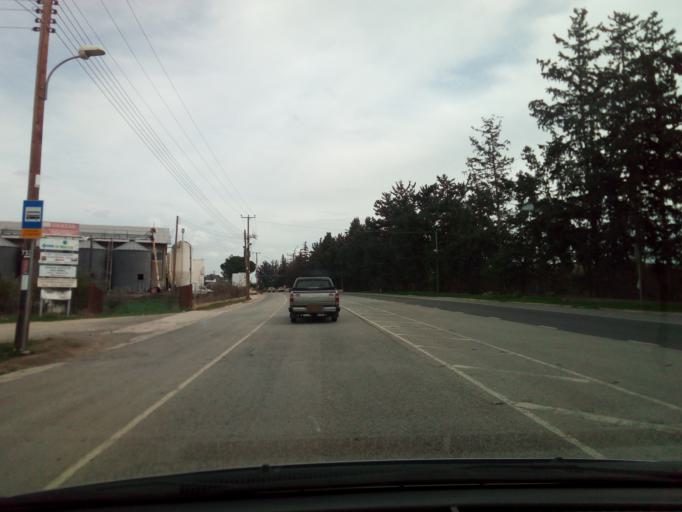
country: CY
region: Lefkosia
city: Akaki
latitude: 35.1352
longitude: 33.1169
